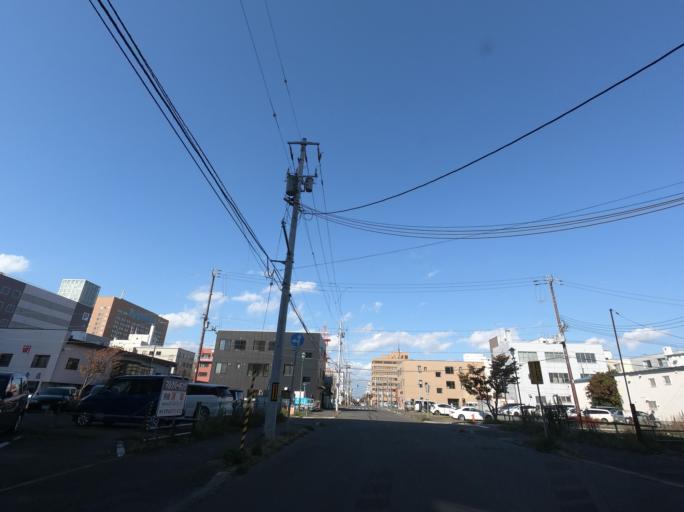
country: JP
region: Hokkaido
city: Kushiro
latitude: 42.9828
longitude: 144.3832
